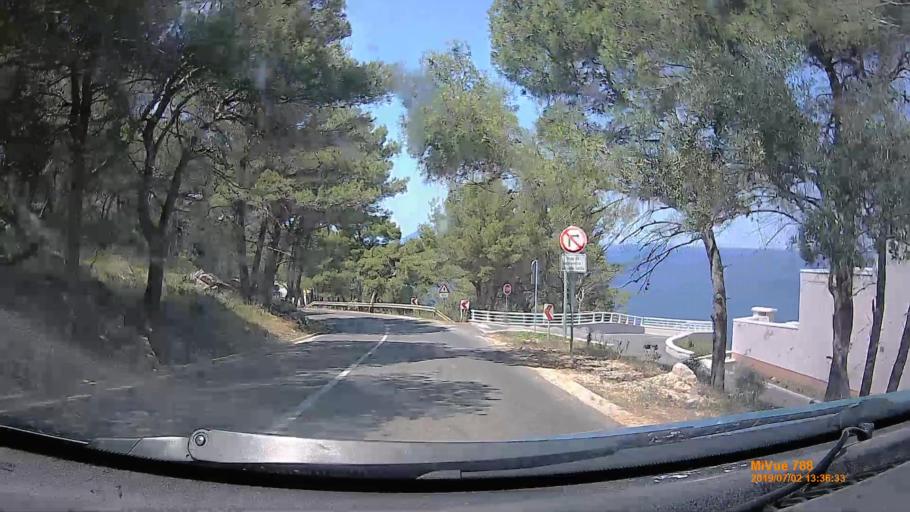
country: HR
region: Primorsko-Goranska
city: Mali Losinj
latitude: 44.5239
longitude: 14.4951
